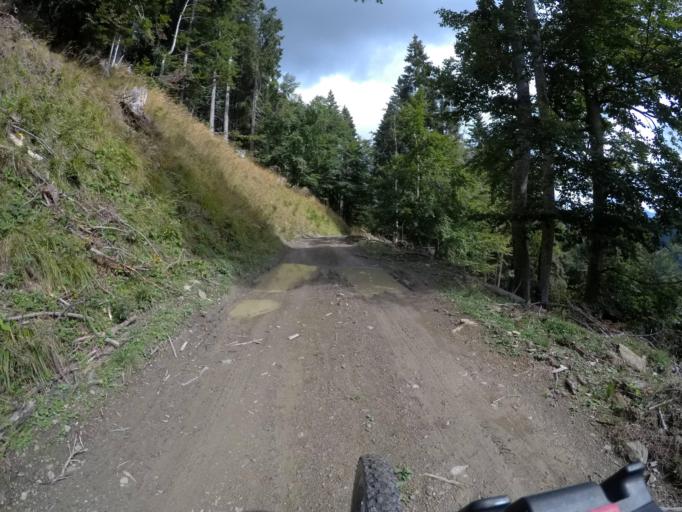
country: IT
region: Friuli Venezia Giulia
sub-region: Provincia di Udine
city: Paularo
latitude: 46.5128
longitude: 13.2061
